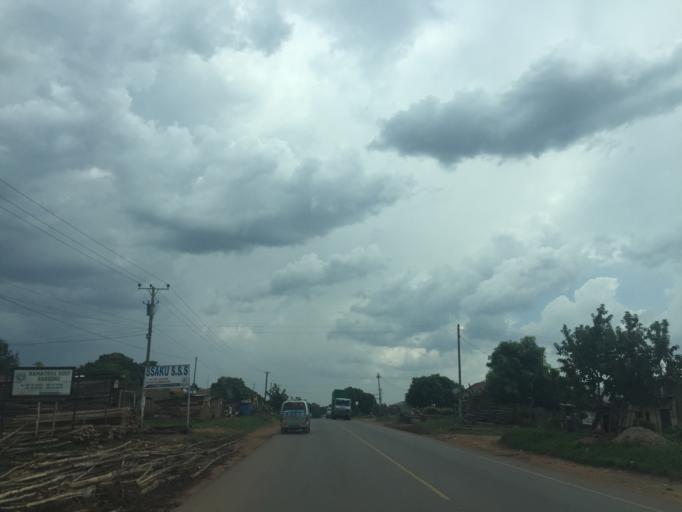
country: UG
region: Central Region
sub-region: Luwero District
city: Wobulenzi
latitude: 0.6794
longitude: 32.5256
